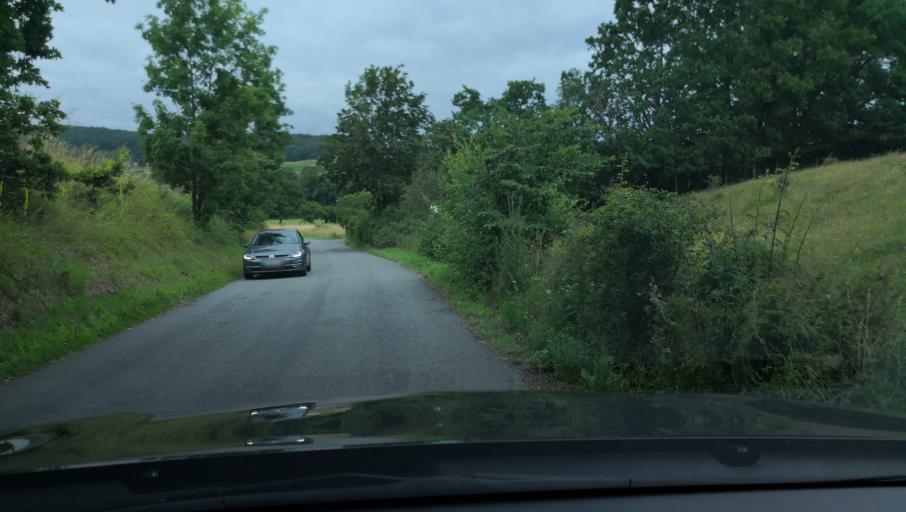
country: SE
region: Skane
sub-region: Simrishamns Kommun
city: Kivik
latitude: 55.7179
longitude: 14.1570
